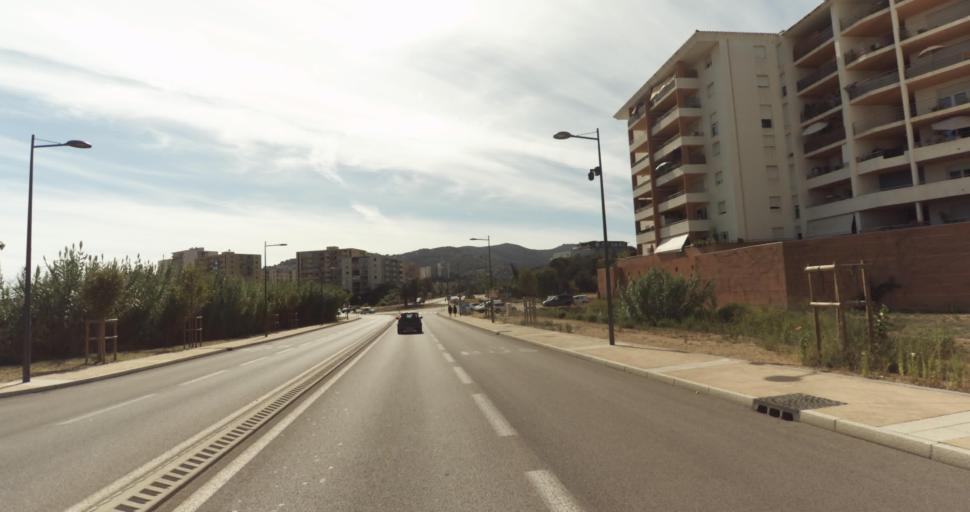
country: FR
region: Corsica
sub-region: Departement de la Corse-du-Sud
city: Ajaccio
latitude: 41.9395
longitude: 8.7430
